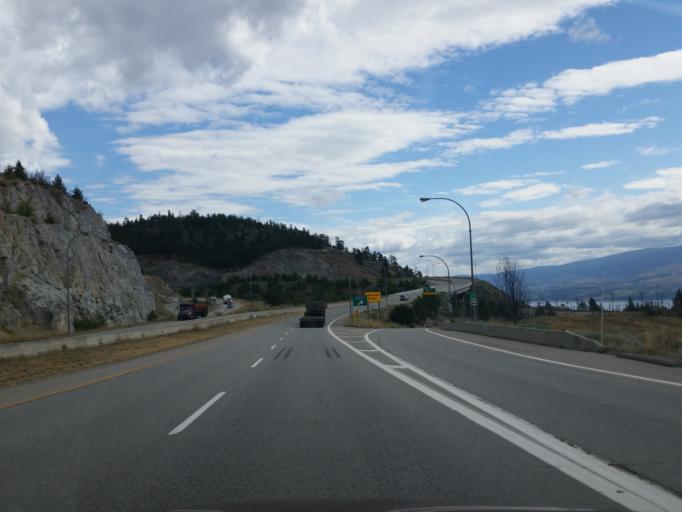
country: CA
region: British Columbia
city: Peachland
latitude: 49.8042
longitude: -119.6693
